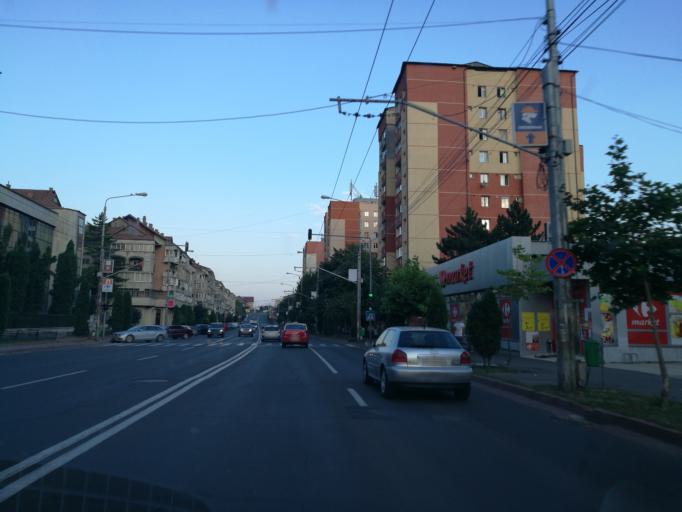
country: RO
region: Neamt
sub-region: Municipiul Piatra-Neamt
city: Valeni
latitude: 46.9239
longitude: 26.3788
